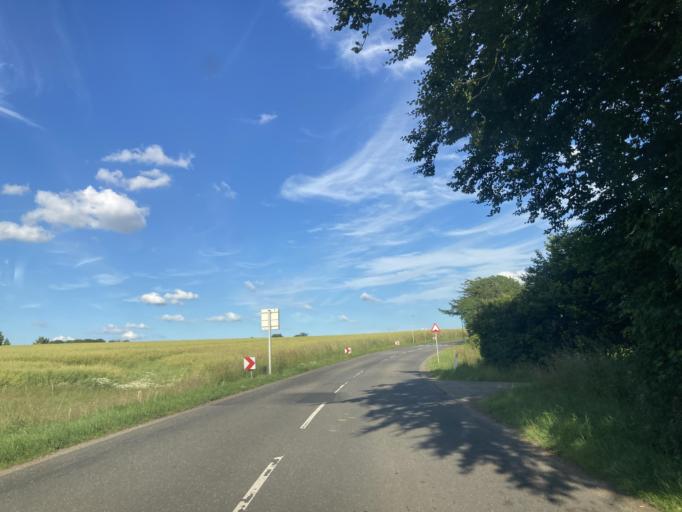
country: DK
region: South Denmark
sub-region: Kolding Kommune
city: Lunderskov
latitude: 55.4872
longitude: 9.3564
